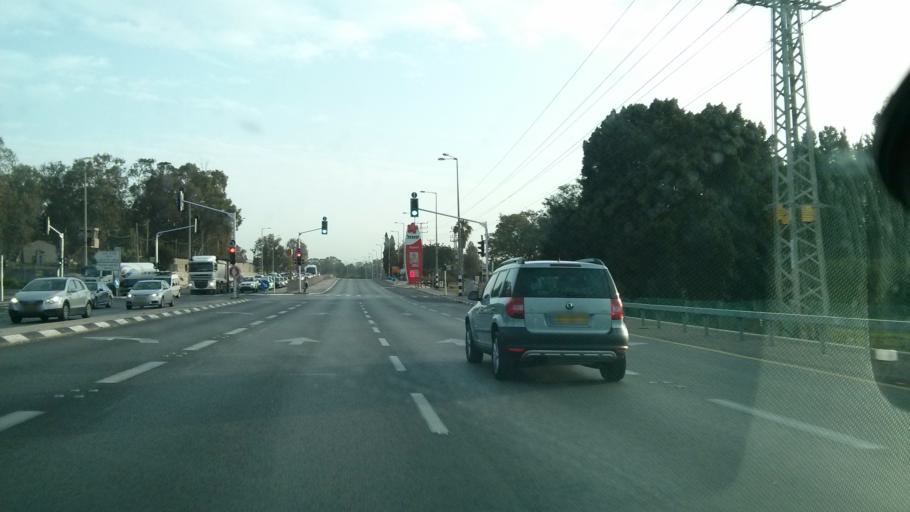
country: IL
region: Central District
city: Elyakhin
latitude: 32.4584
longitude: 34.9858
